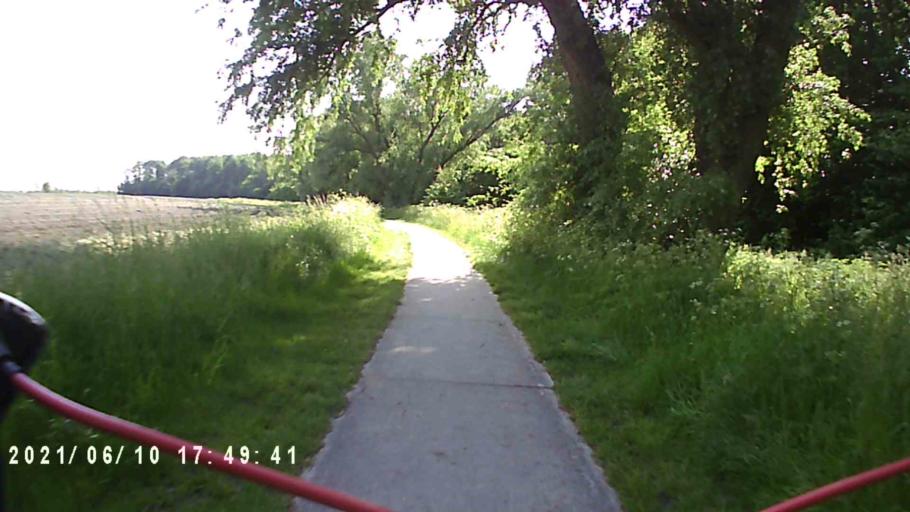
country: NL
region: Groningen
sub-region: Gemeente De Marne
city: Ulrum
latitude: 53.3357
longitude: 6.3133
